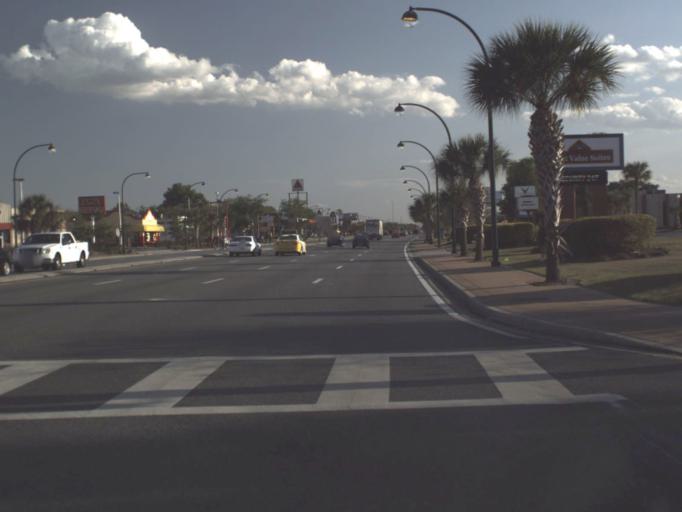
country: US
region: Florida
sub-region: Orange County
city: Sky Lake
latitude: 28.4631
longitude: -81.3974
